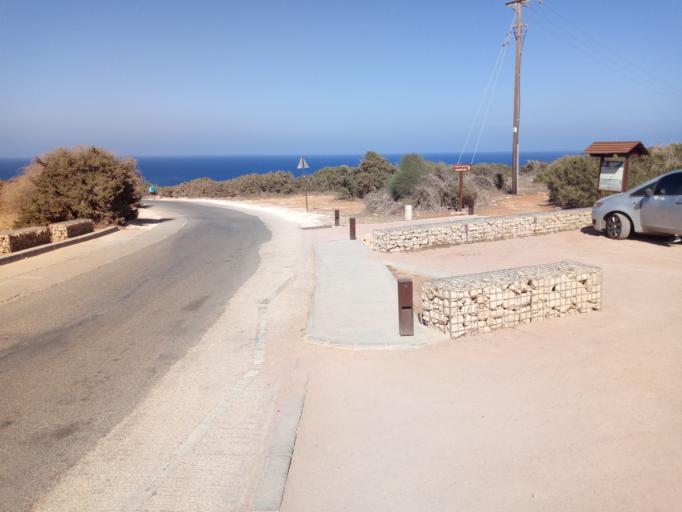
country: CY
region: Ammochostos
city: Protaras
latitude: 34.9705
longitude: 34.0709
